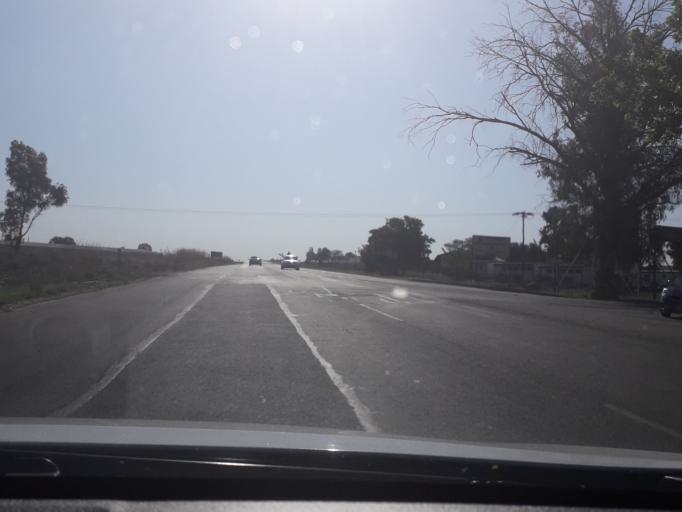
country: ZA
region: Gauteng
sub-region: City of Johannesburg Metropolitan Municipality
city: Diepsloot
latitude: -25.9670
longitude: 27.9318
